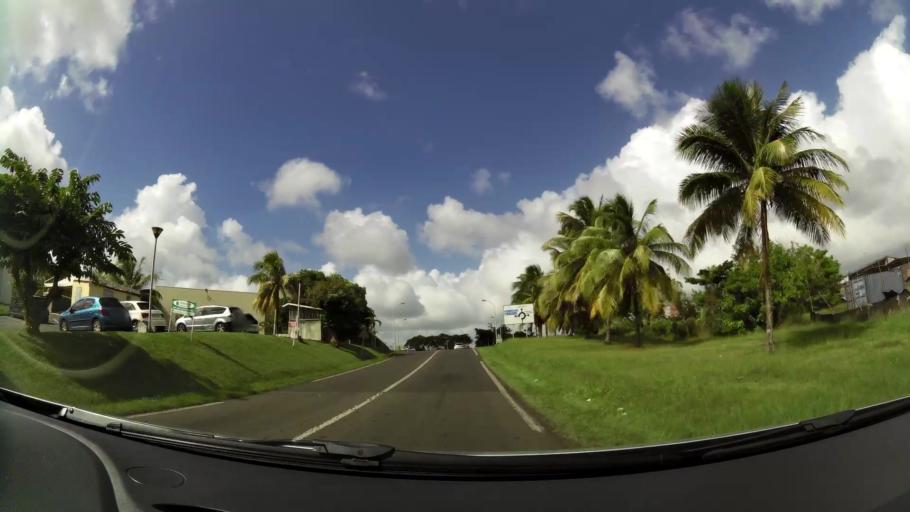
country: MQ
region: Martinique
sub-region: Martinique
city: Le Lamentin
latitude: 14.6215
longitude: -60.9882
